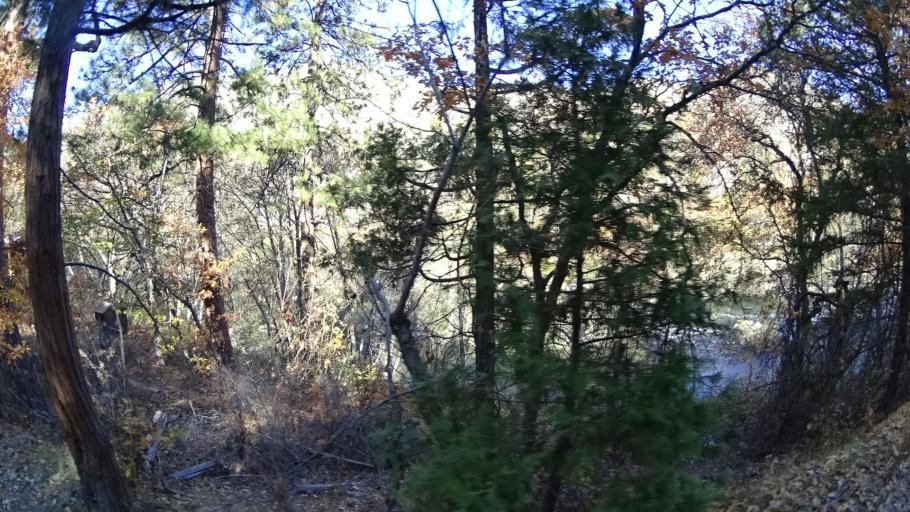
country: US
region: California
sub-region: Siskiyou County
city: Yreka
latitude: 41.8556
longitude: -122.7598
